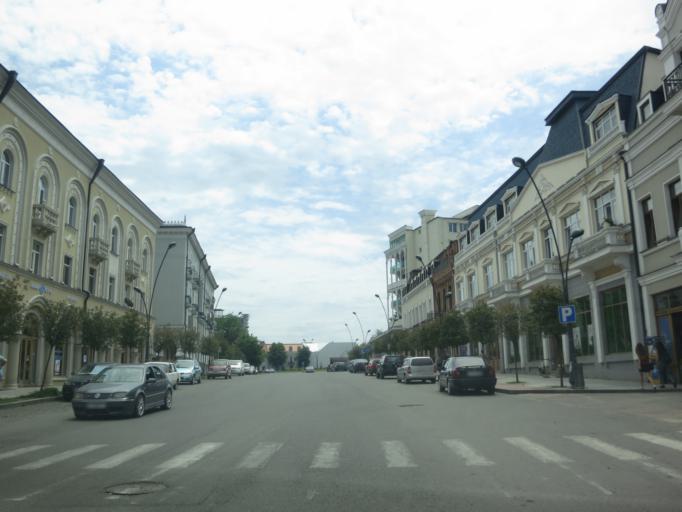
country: GE
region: Kakheti
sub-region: Telavi
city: Telavi
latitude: 41.9189
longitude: 45.4721
